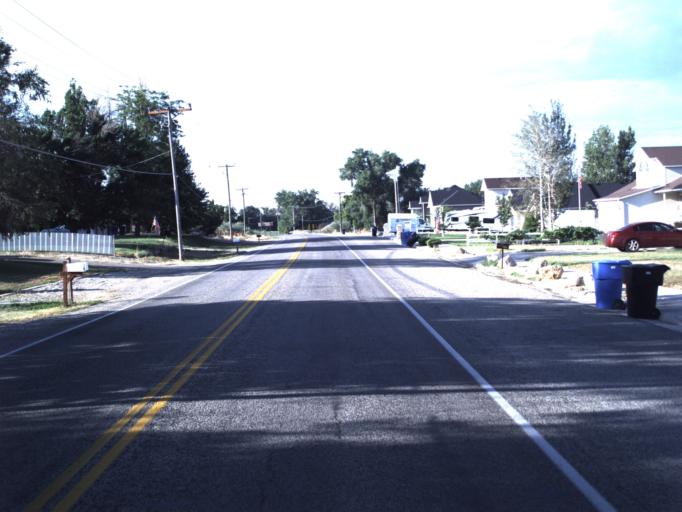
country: US
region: Utah
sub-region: Weber County
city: Plain City
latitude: 41.2839
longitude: -112.0934
